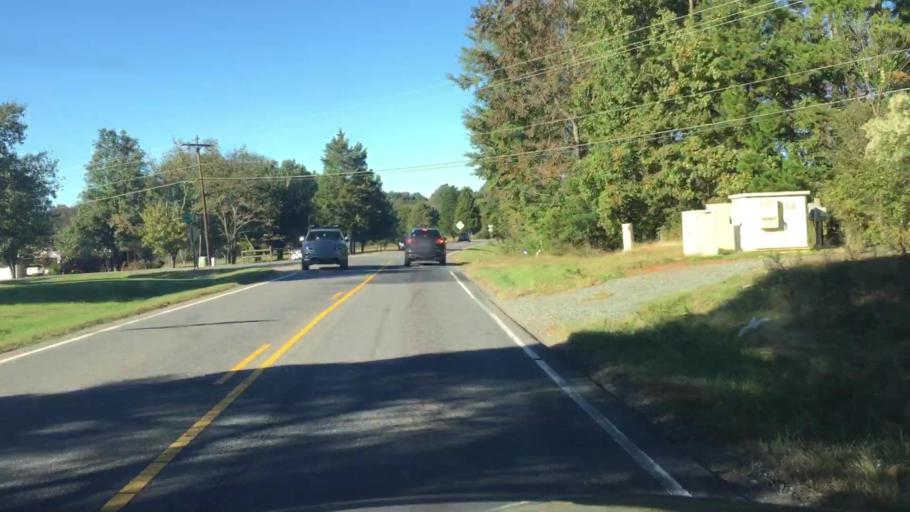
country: US
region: North Carolina
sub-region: Gaston County
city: Davidson
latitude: 35.5190
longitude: -80.7704
